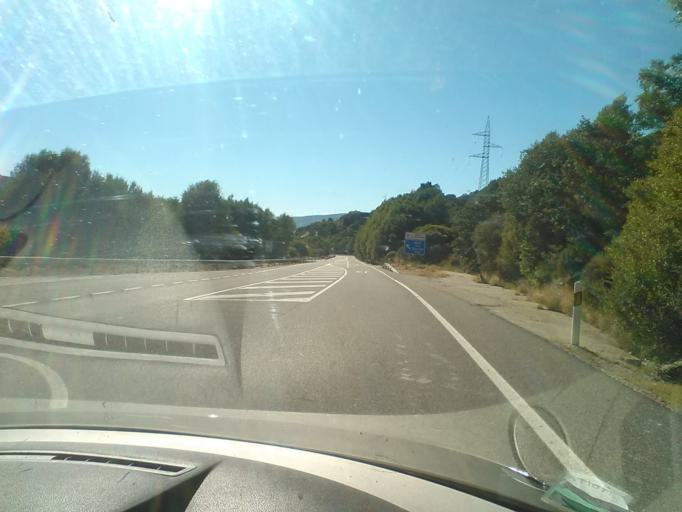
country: ES
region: Castille and Leon
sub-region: Provincia de Zamora
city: Lubian
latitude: 42.0352
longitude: -6.8430
